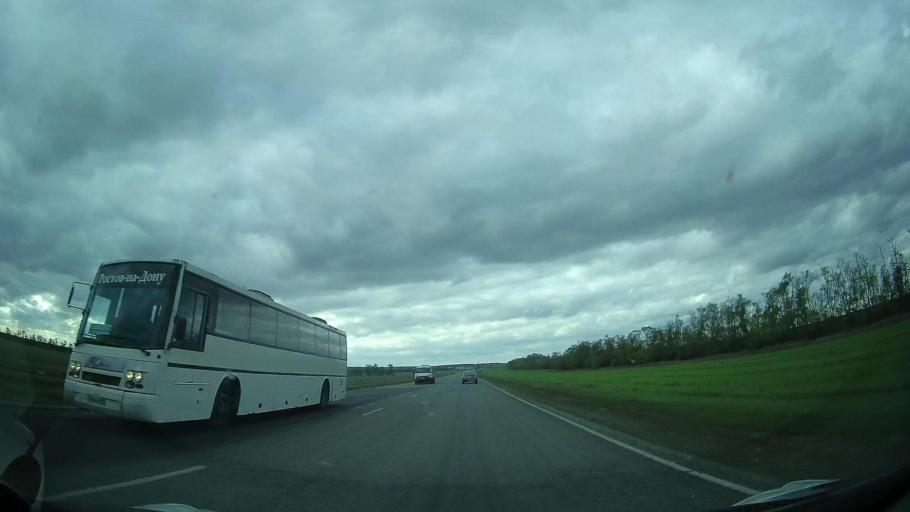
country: RU
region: Rostov
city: Kagal'nitskaya
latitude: 46.8668
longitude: 40.1746
